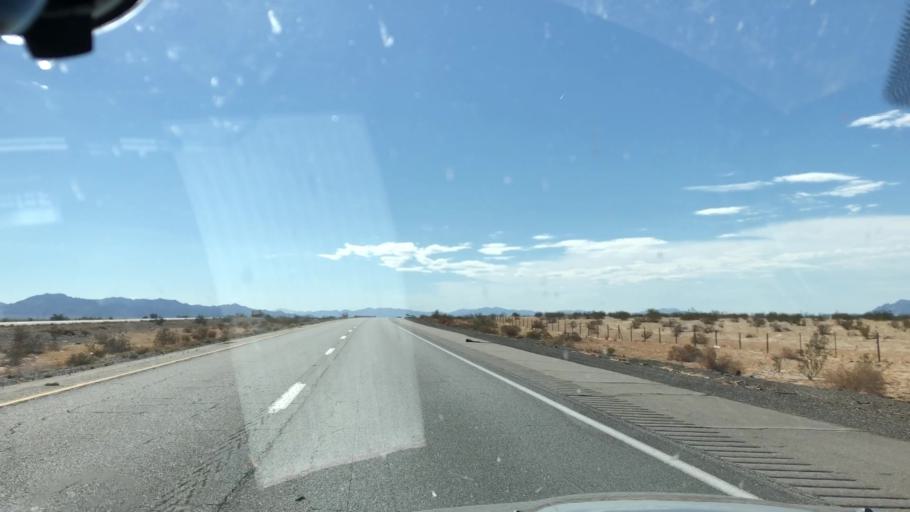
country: US
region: California
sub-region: Riverside County
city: Mesa Verde
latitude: 33.6440
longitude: -115.1125
